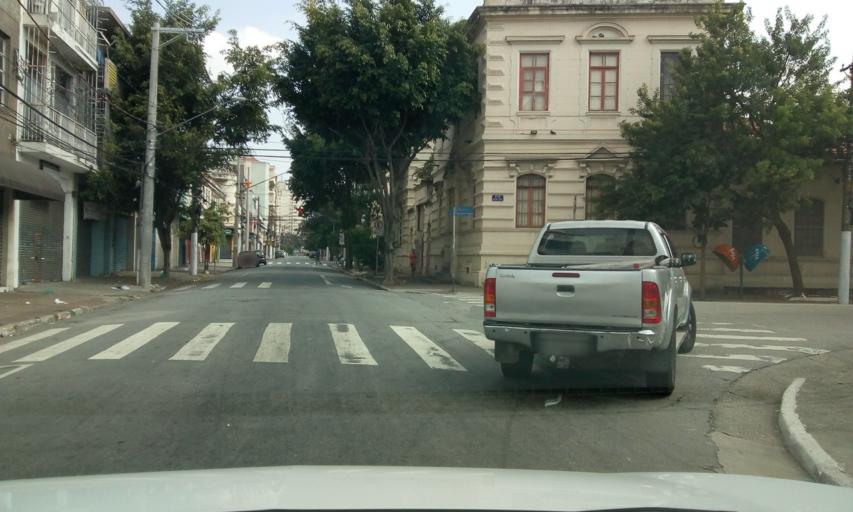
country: BR
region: Sao Paulo
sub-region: Sao Paulo
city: Sao Paulo
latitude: -23.5263
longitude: -46.6419
